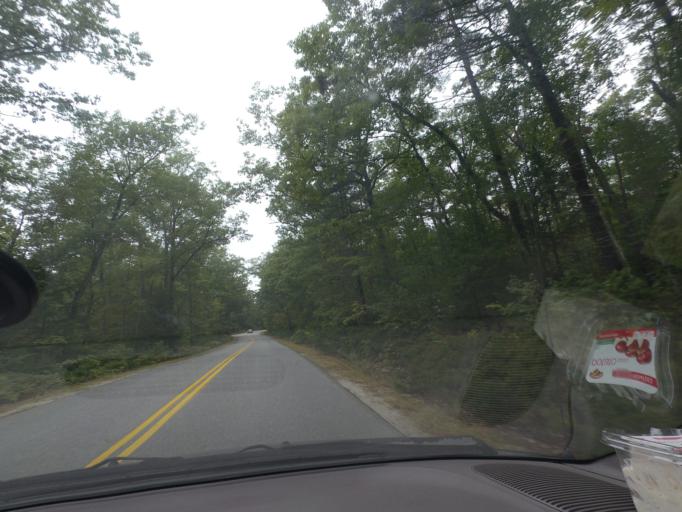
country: US
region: Maine
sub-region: Cumberland County
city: Raymond
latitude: 43.8894
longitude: -70.4278
